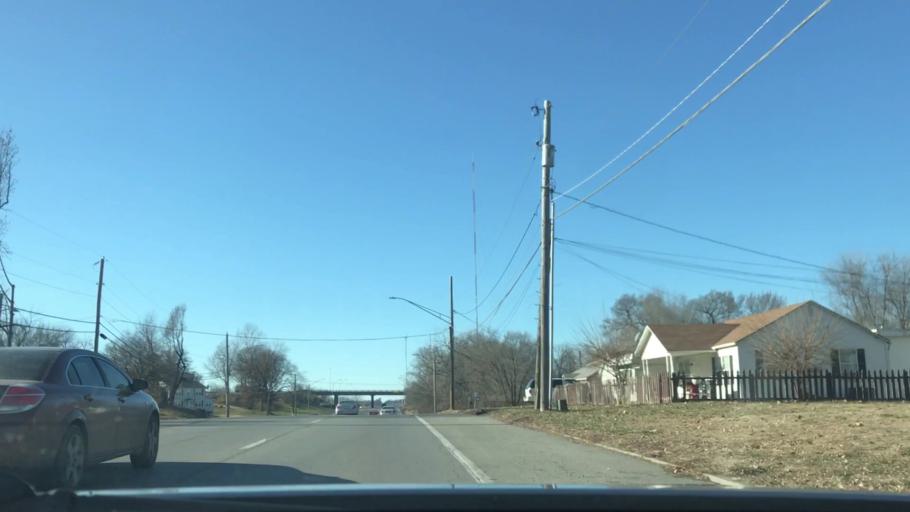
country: US
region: Missouri
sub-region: Jackson County
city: Sugar Creek
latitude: 39.0813
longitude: -94.4673
